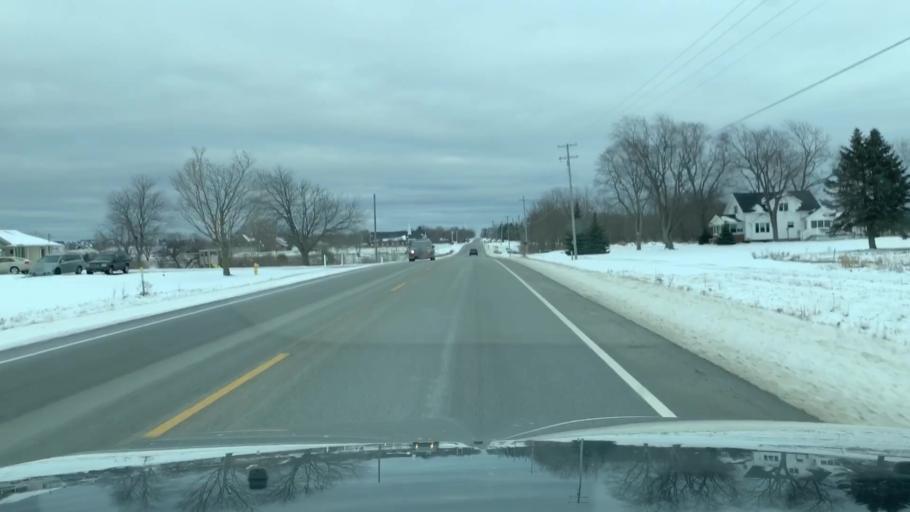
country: US
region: Michigan
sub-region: Ottawa County
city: Zeeland
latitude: 42.8121
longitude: -85.9578
